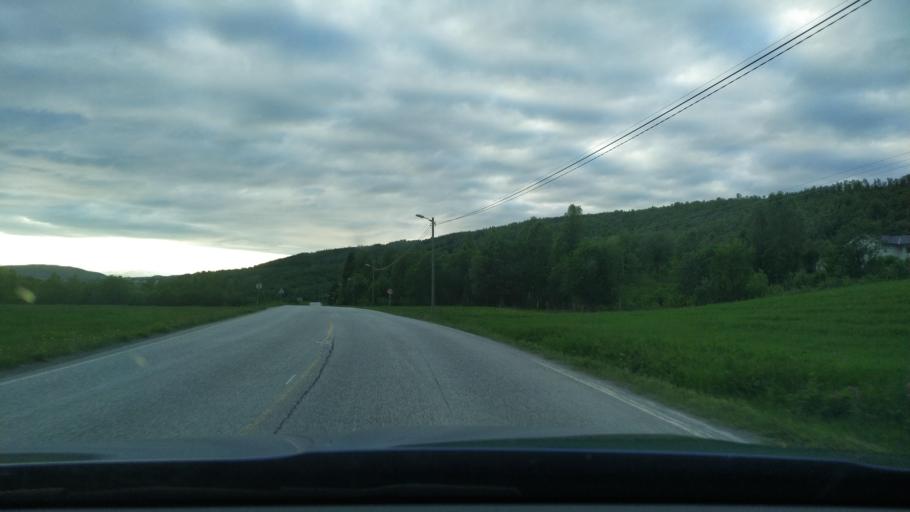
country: NO
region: Troms
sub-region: Sorreisa
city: Sorreisa
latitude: 69.1215
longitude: 18.2211
